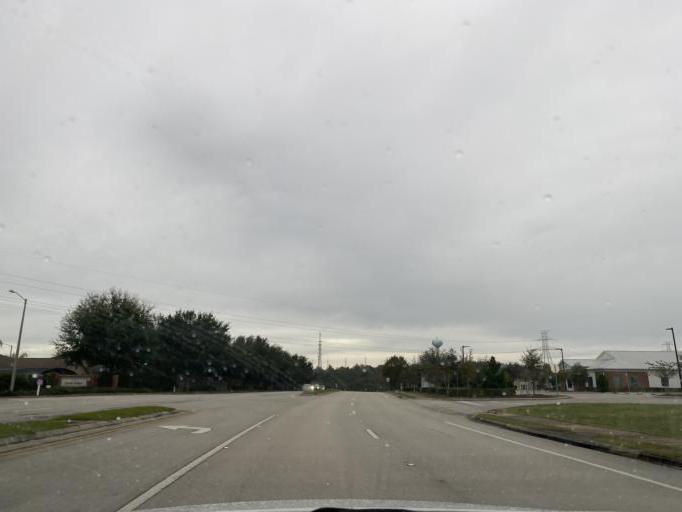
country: US
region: Florida
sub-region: Lake County
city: Minneola
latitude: 28.5432
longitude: -81.7091
